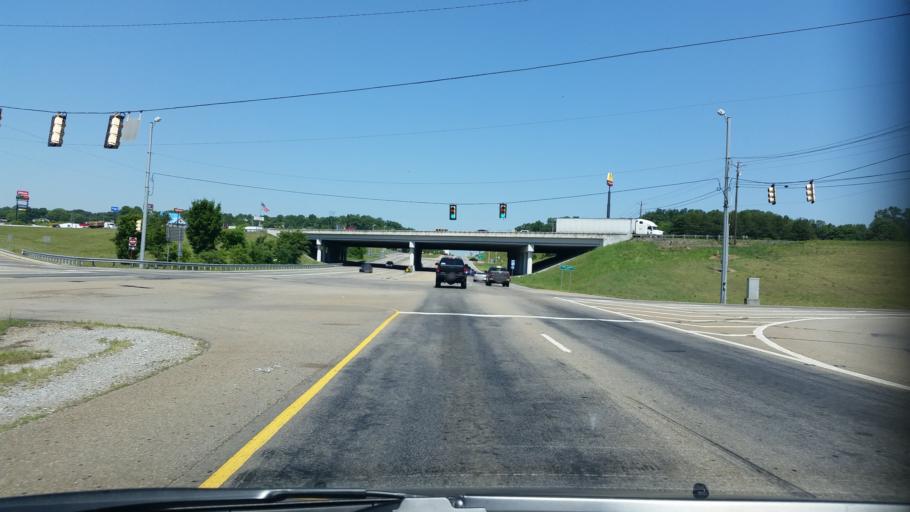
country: US
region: Tennessee
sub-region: Jefferson County
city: Dandridge
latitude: 36.0378
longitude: -83.4383
